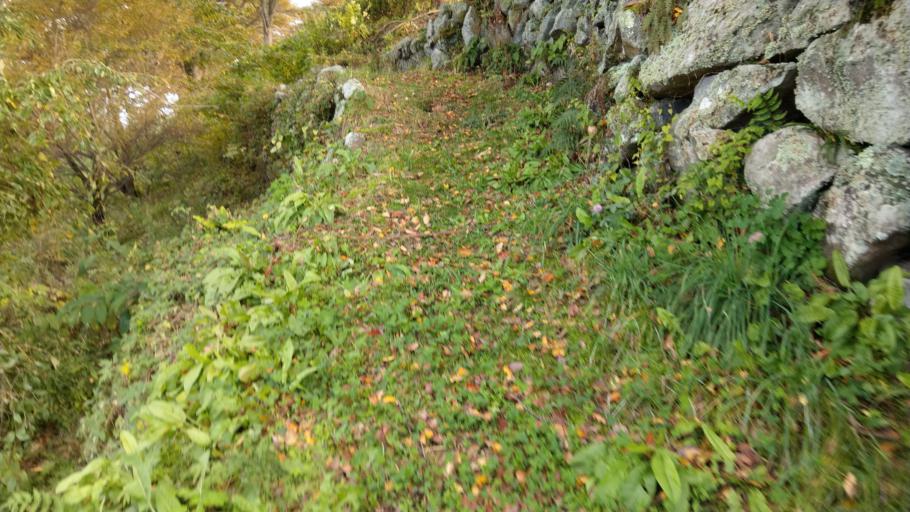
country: JP
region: Nagano
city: Komoro
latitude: 36.3460
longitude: 138.4175
